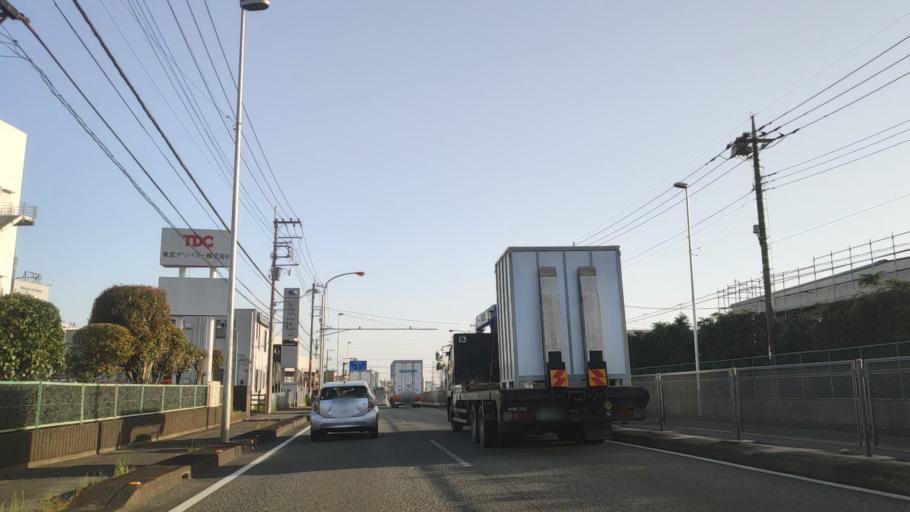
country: JP
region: Kanagawa
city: Zama
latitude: 35.4693
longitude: 139.3681
